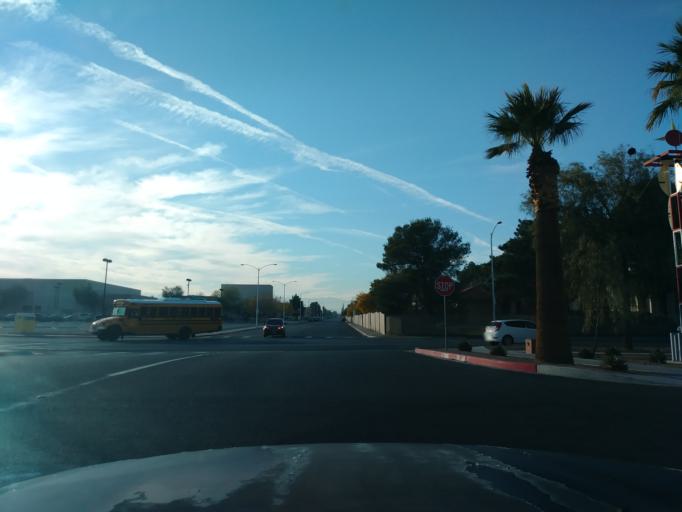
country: US
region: Nevada
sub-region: Clark County
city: Spring Valley
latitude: 36.1555
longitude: -115.2342
